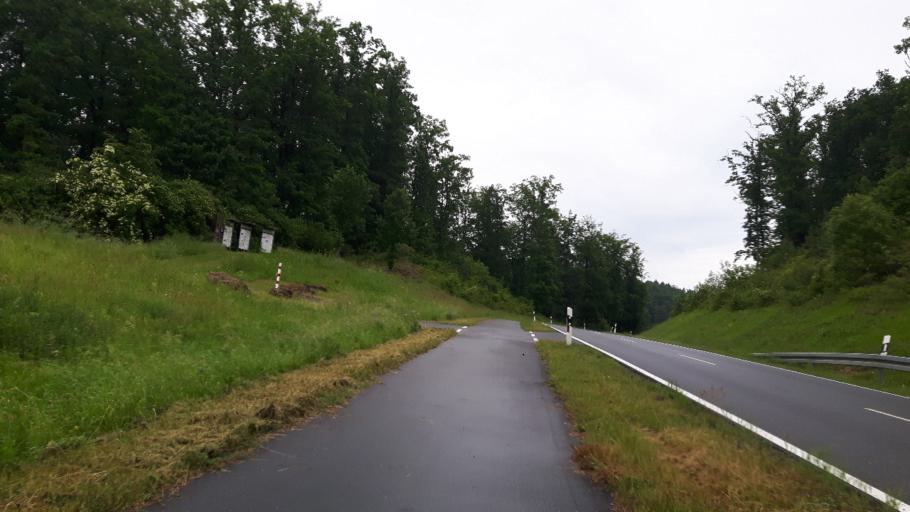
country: DE
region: Bavaria
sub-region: Regierungsbezirk Unterfranken
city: Uchtelhausen
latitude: 50.1004
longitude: 10.2503
